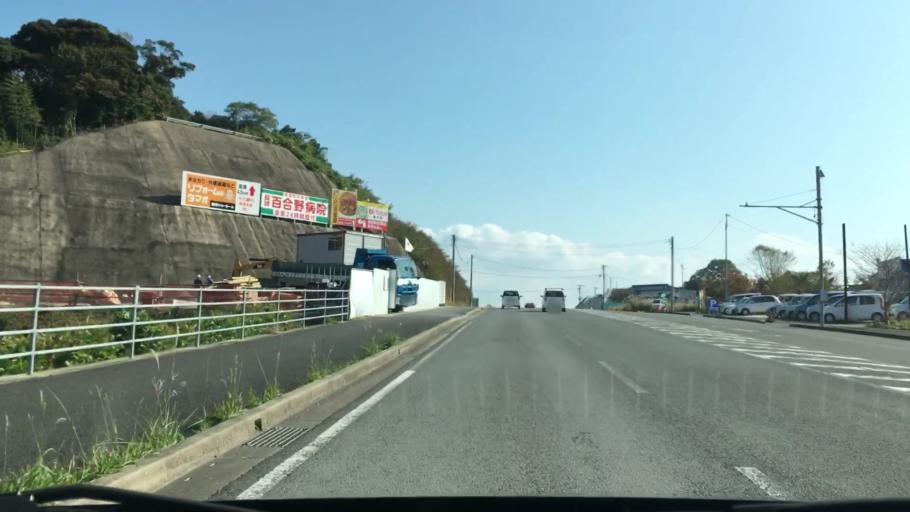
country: JP
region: Nagasaki
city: Togitsu
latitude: 32.8590
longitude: 129.8171
